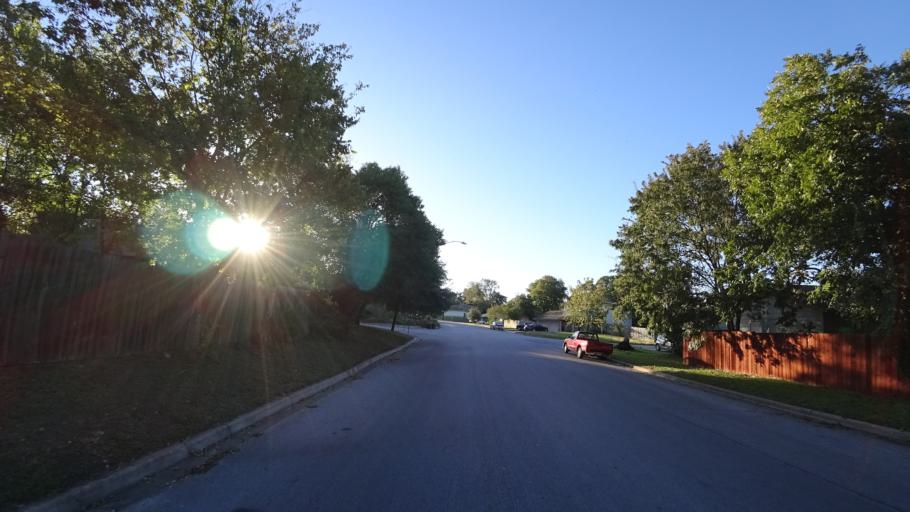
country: US
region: Texas
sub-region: Travis County
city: Austin
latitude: 30.2985
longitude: -97.6797
